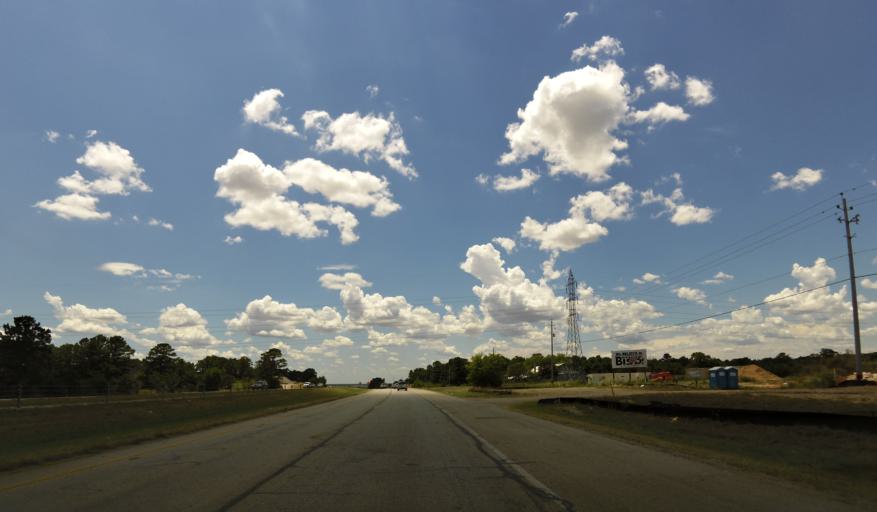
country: US
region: Texas
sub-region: Bastrop County
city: Bastrop
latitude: 30.1050
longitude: -97.2937
